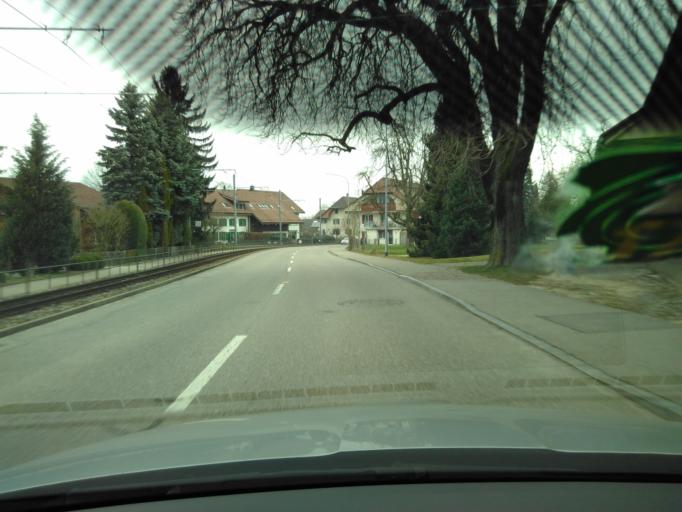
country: CH
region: Aargau
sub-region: Bezirk Kulm
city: Schoftland
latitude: 47.3171
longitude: 8.0529
